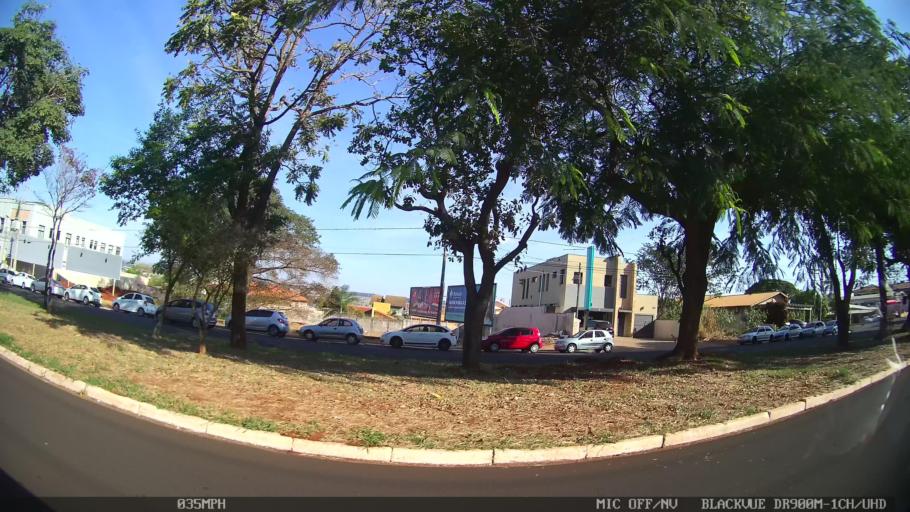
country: BR
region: Sao Paulo
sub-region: Ribeirao Preto
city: Ribeirao Preto
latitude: -21.2047
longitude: -47.7740
